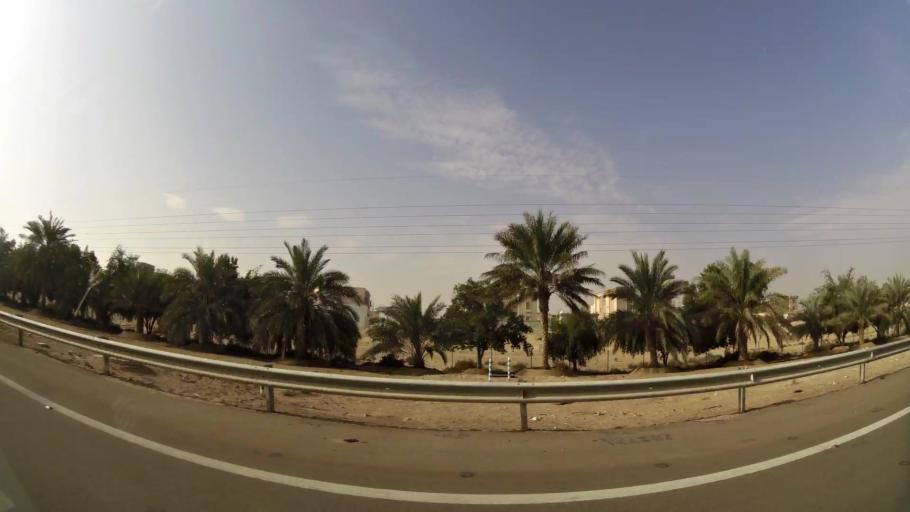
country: AE
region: Abu Dhabi
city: Abu Dhabi
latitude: 24.2724
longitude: 54.6588
